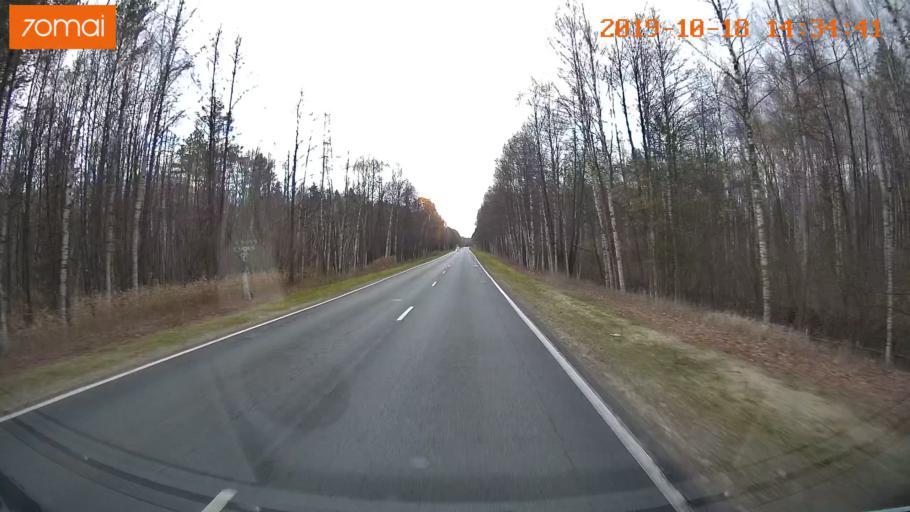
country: RU
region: Vladimir
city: Velikodvorskiy
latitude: 55.2148
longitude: 40.6209
